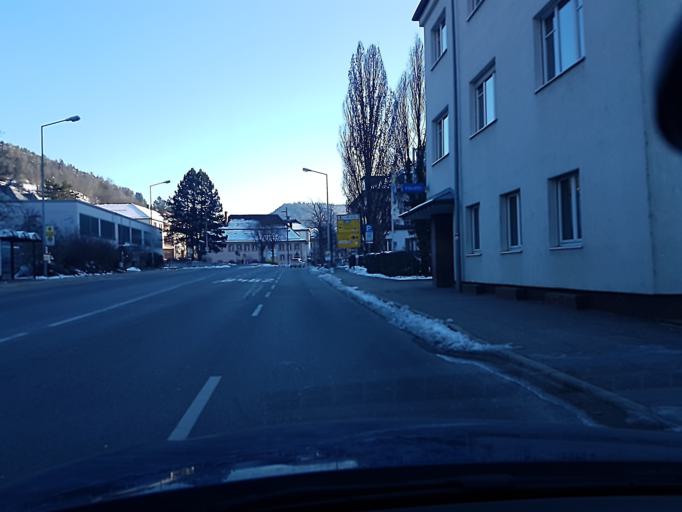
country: DE
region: Baden-Wuerttemberg
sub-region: Freiburg Region
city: Schramberg
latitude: 48.2292
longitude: 8.3841
